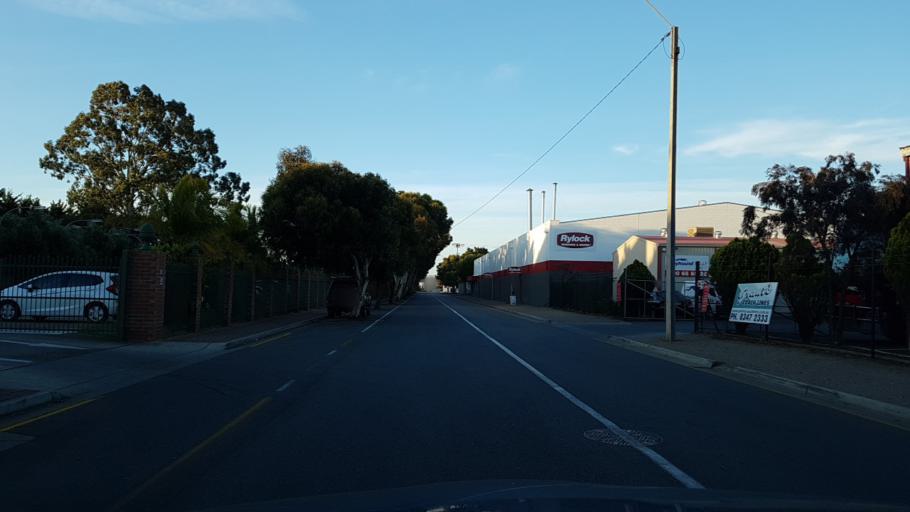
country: AU
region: South Australia
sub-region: Charles Sturt
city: Woodville North
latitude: -34.8681
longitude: 138.5383
